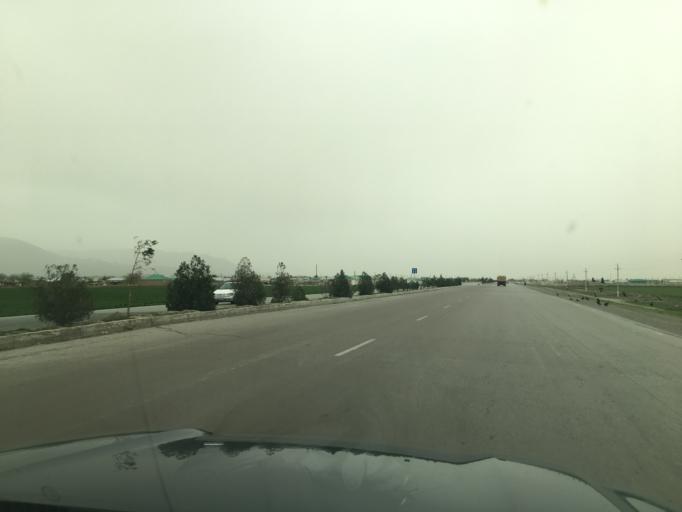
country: TM
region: Ahal
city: Baharly
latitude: 38.3923
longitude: 57.4839
